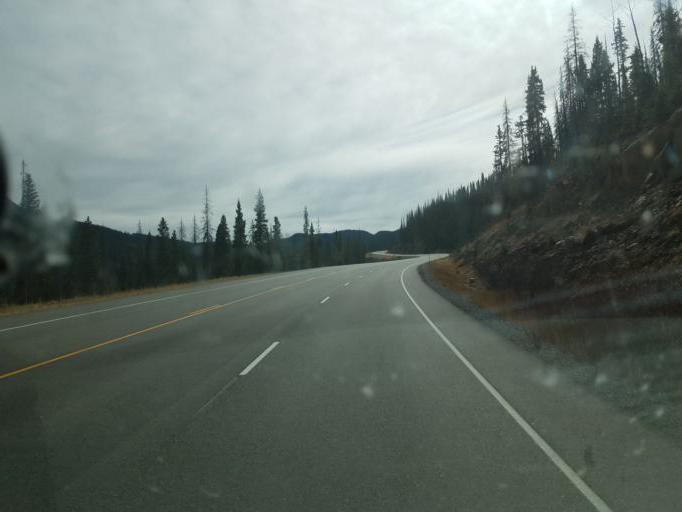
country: US
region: Colorado
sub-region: Archuleta County
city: Pagosa Springs
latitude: 37.5023
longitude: -106.7717
